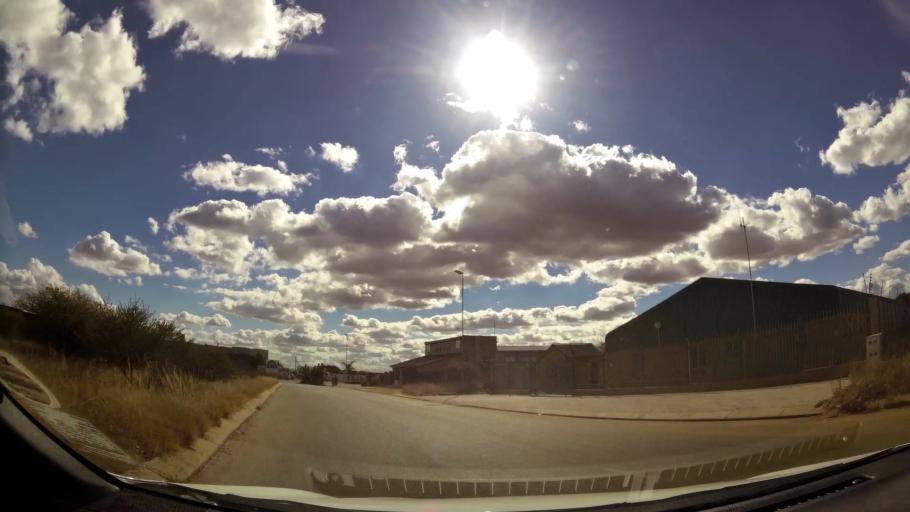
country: ZA
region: Limpopo
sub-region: Capricorn District Municipality
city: Polokwane
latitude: -23.8647
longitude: 29.4820
